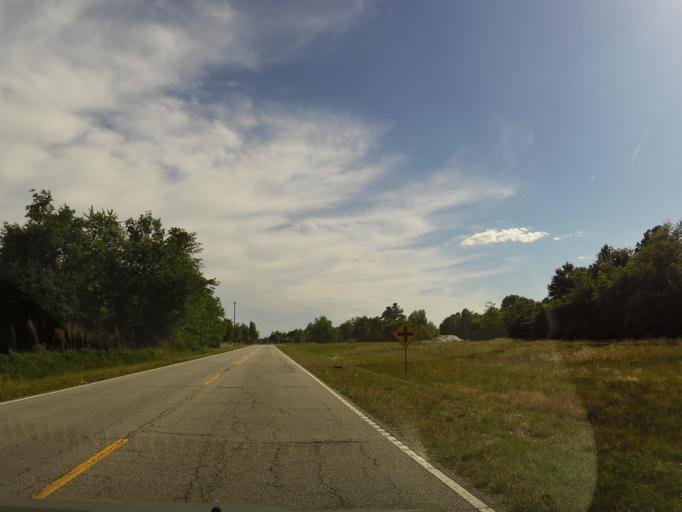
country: US
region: South Carolina
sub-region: Allendale County
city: Fairfax
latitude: 33.0415
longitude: -81.2207
